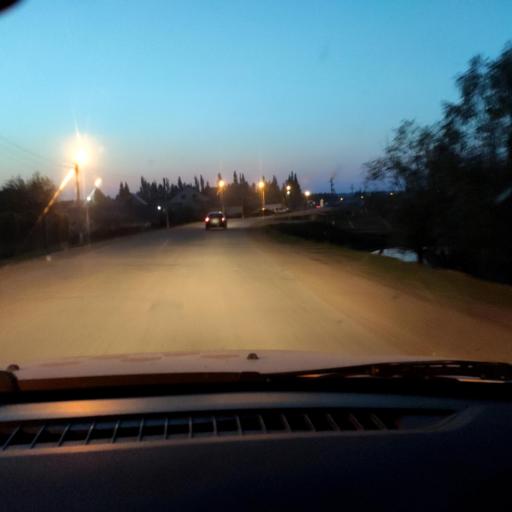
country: RU
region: Bashkortostan
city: Karmaskaly
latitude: 54.3630
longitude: 56.1584
